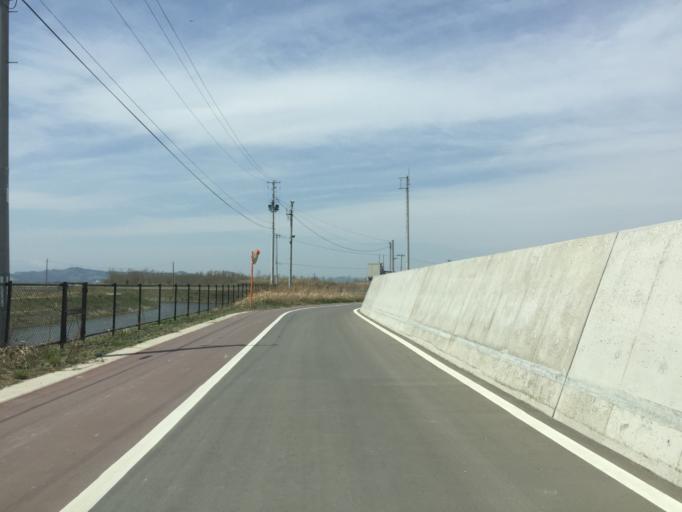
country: JP
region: Miyagi
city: Watari
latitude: 38.0278
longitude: 140.9149
